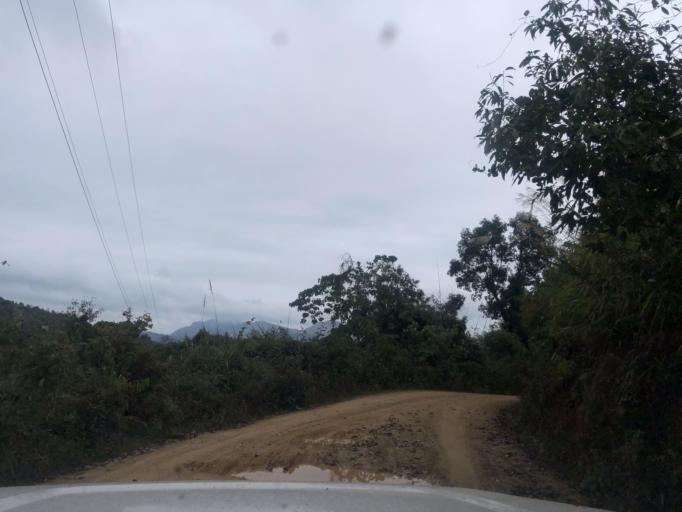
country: LA
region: Phongsali
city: Khoa
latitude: 21.2580
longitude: 102.5896
